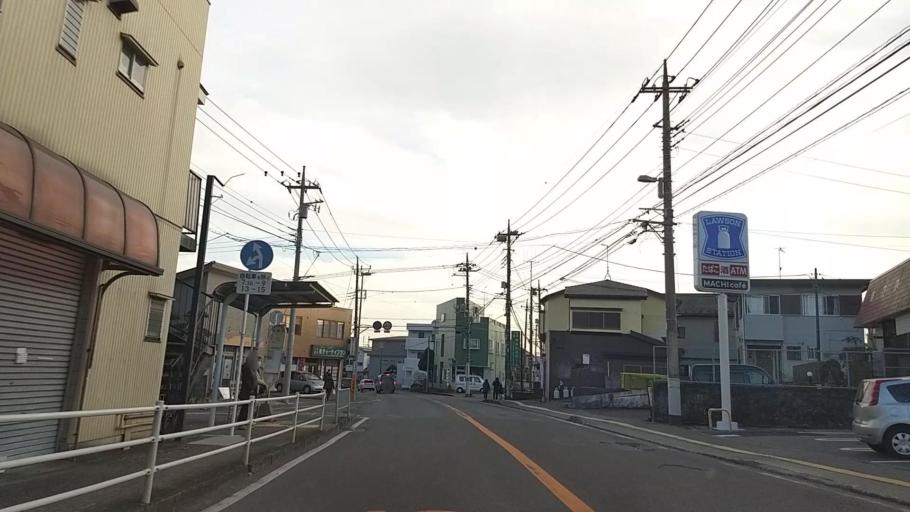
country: JP
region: Kanagawa
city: Atsugi
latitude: 35.4693
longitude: 139.3498
